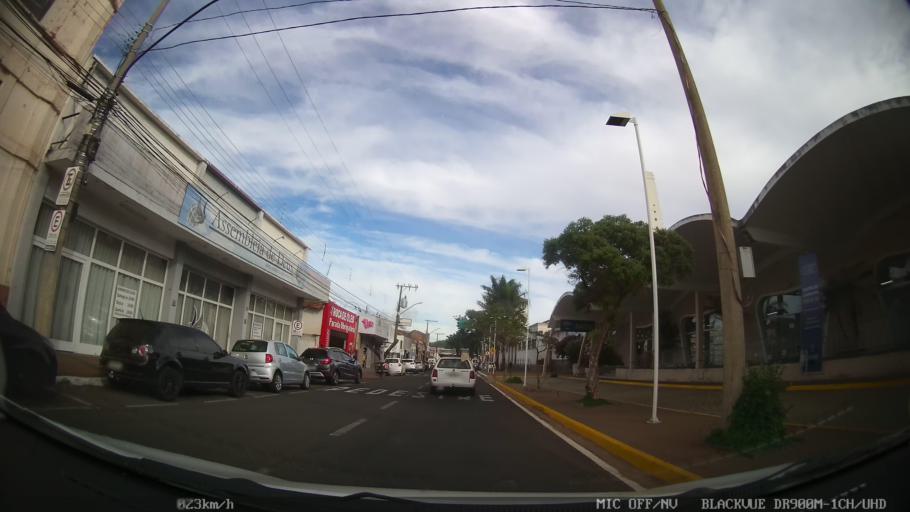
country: BR
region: Sao Paulo
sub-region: Catanduva
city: Catanduva
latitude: -21.1308
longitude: -48.9692
